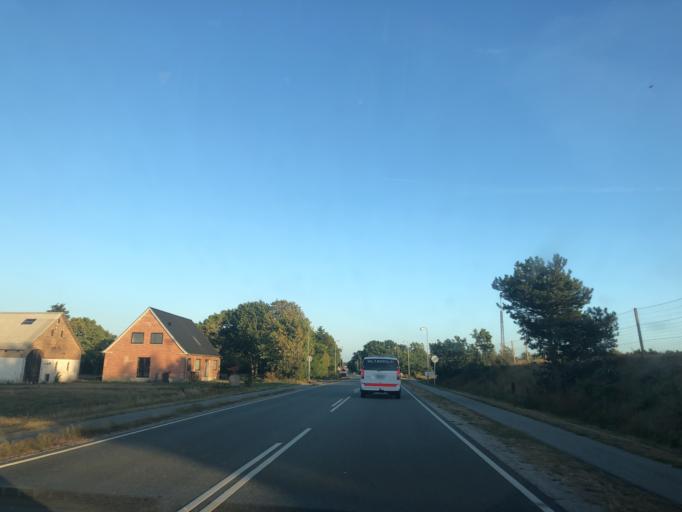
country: DK
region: North Denmark
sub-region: Frederikshavn Kommune
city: Strandby
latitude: 57.5396
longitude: 10.4161
